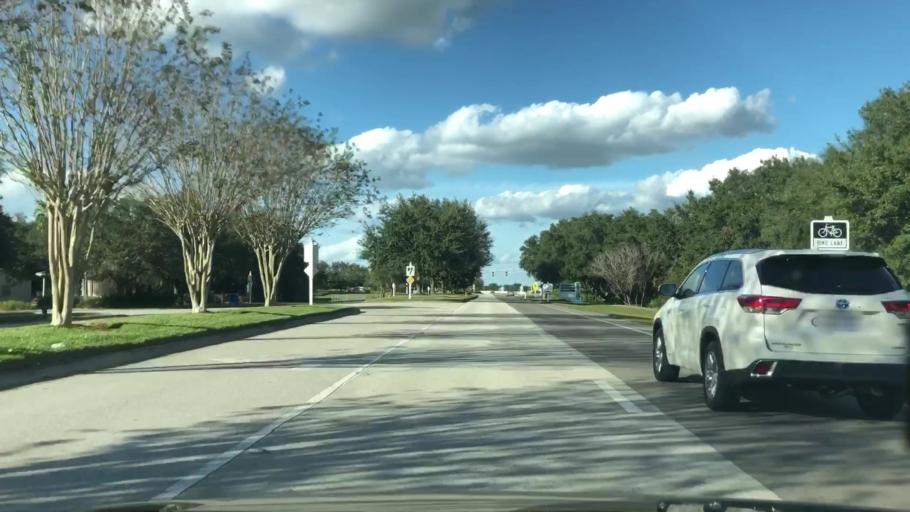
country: US
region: Florida
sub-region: Sarasota County
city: The Meadows
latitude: 27.3934
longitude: -82.3983
